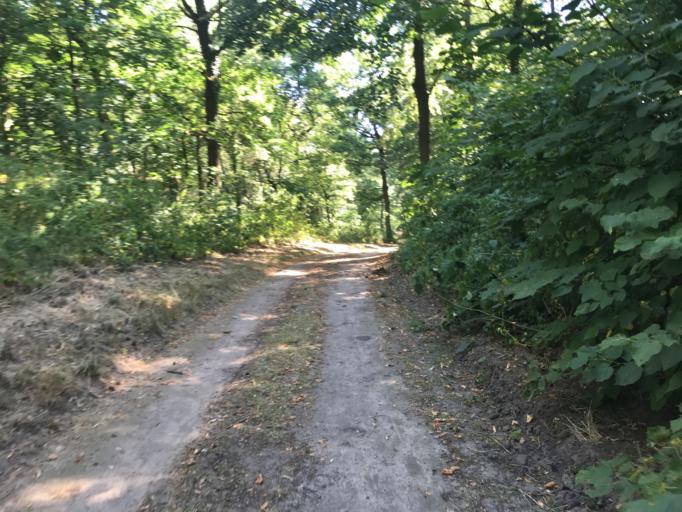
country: DE
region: Rheinland-Pfalz
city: Budenheim
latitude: 50.0137
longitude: 8.1560
